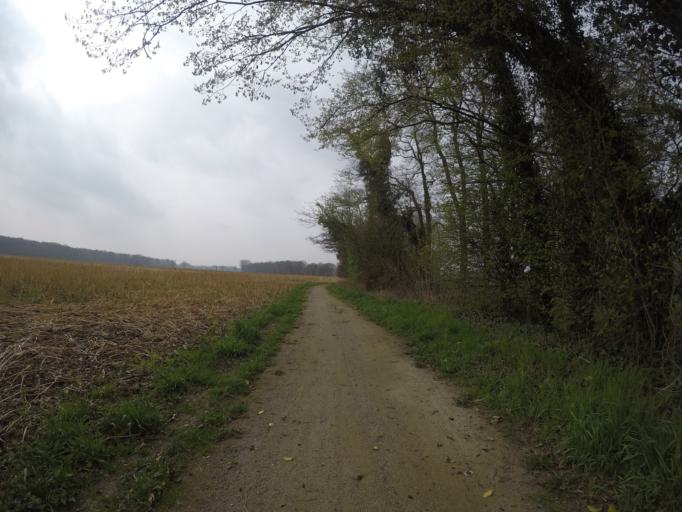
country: DE
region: North Rhine-Westphalia
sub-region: Regierungsbezirk Dusseldorf
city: Bocholt
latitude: 51.8869
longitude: 6.6481
